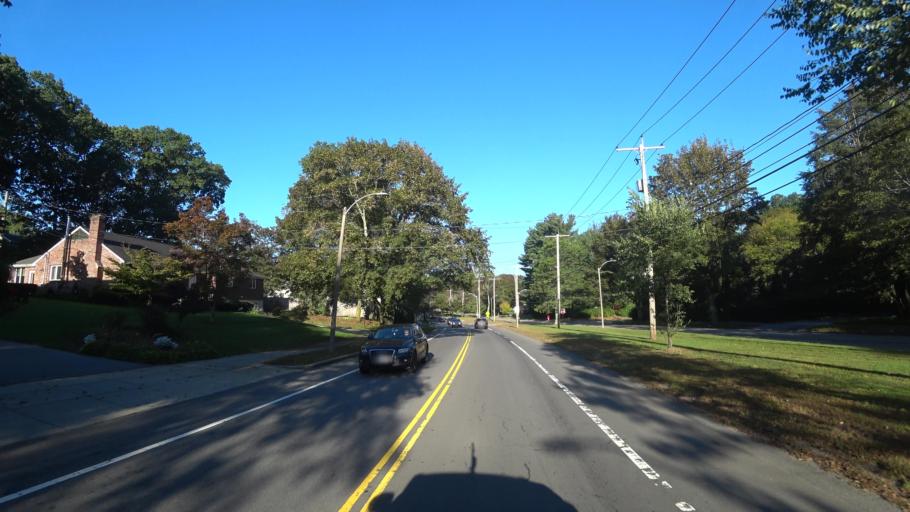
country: US
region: Massachusetts
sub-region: Middlesex County
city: Newton
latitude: 42.3387
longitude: -71.2275
